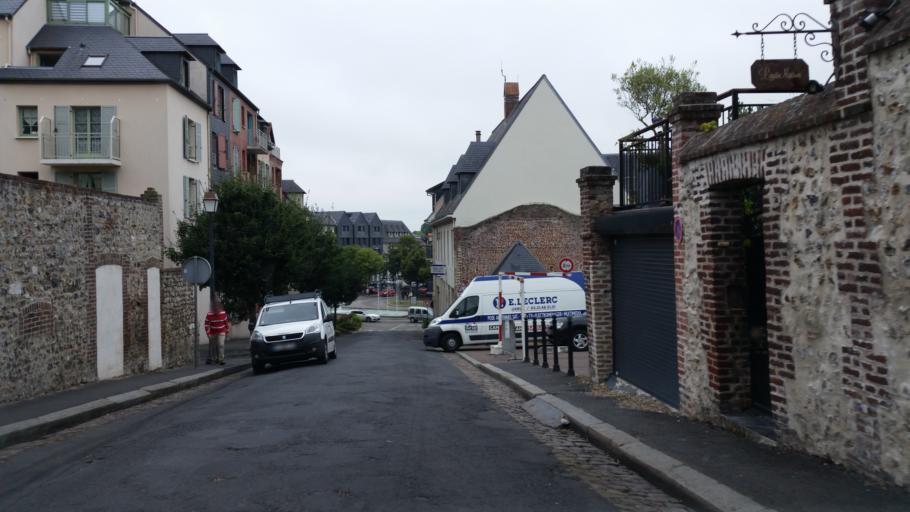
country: FR
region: Lower Normandy
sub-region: Departement du Calvados
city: Honfleur
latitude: 49.4177
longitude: 0.2364
